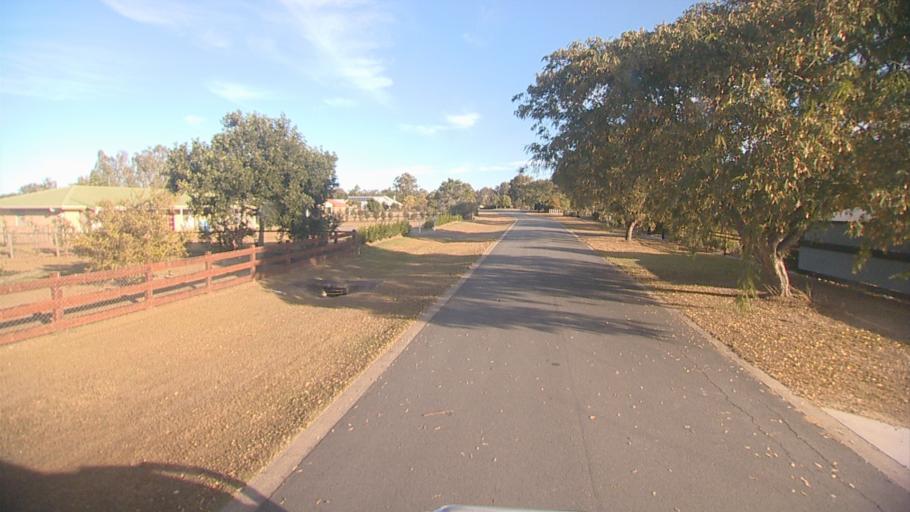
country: AU
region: Queensland
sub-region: Logan
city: North Maclean
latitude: -27.8239
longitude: 153.0078
